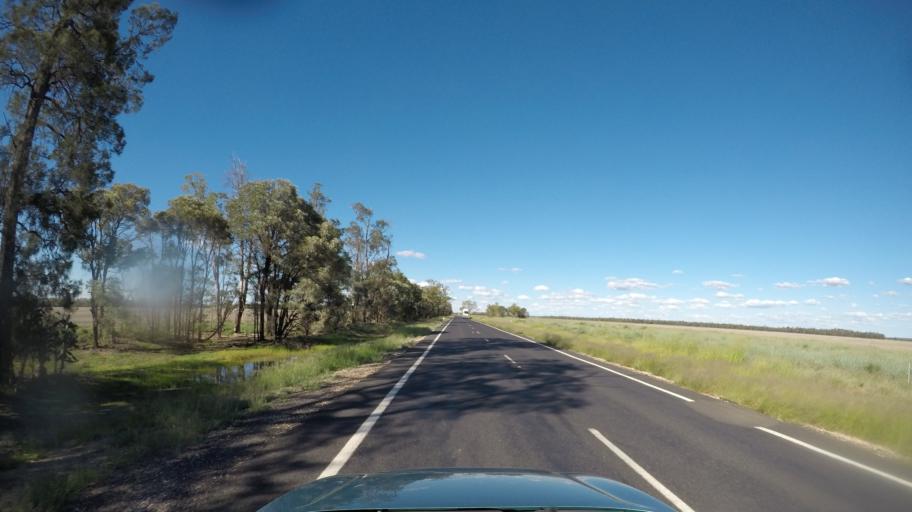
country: AU
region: Queensland
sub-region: Goondiwindi
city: Goondiwindi
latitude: -28.1430
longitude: 150.6892
